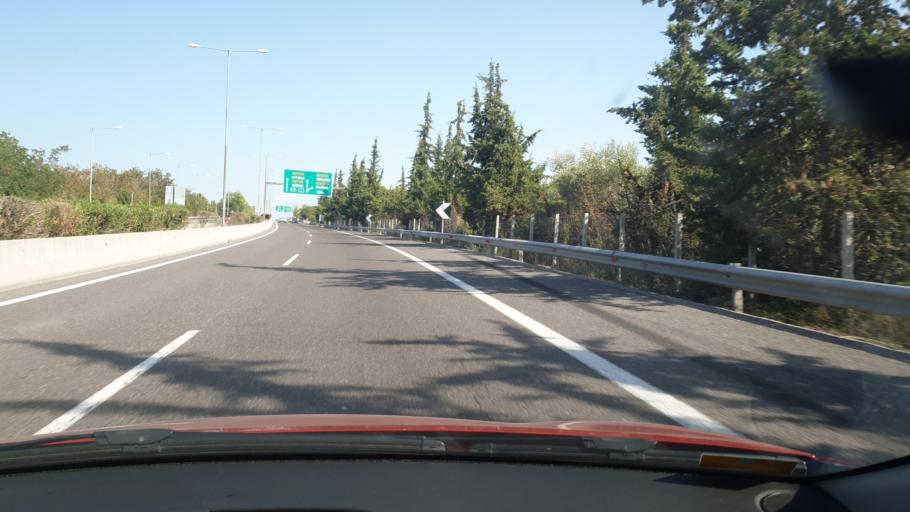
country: GR
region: Central Greece
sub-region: Nomos Fthiotidos
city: Martinon
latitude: 38.5982
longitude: 23.1832
